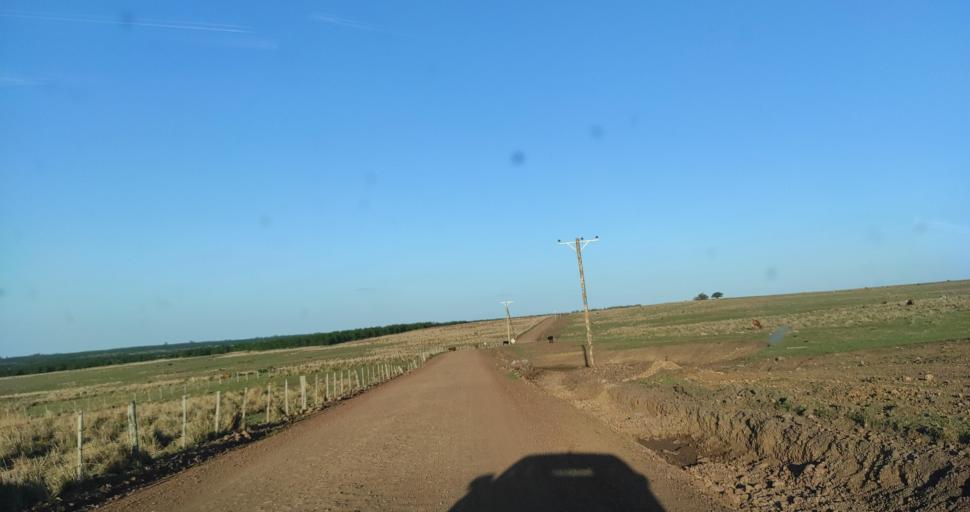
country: PY
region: Itapua
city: Carmen del Parana
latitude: -27.4122
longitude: -56.1437
